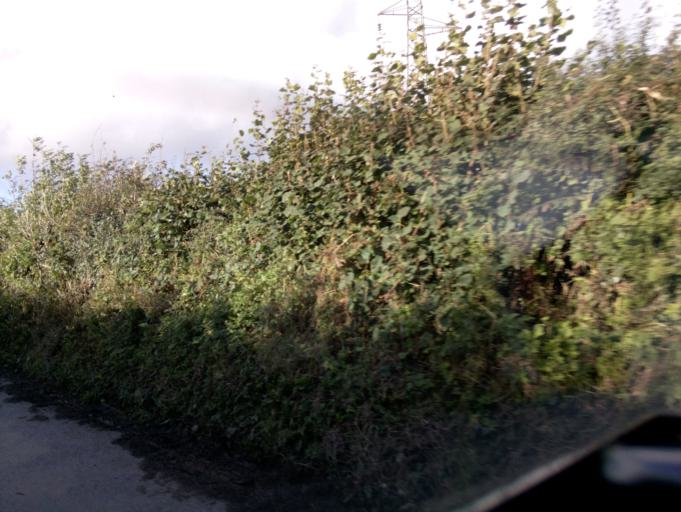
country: GB
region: England
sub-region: Devon
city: Totnes
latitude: 50.3559
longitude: -3.7272
